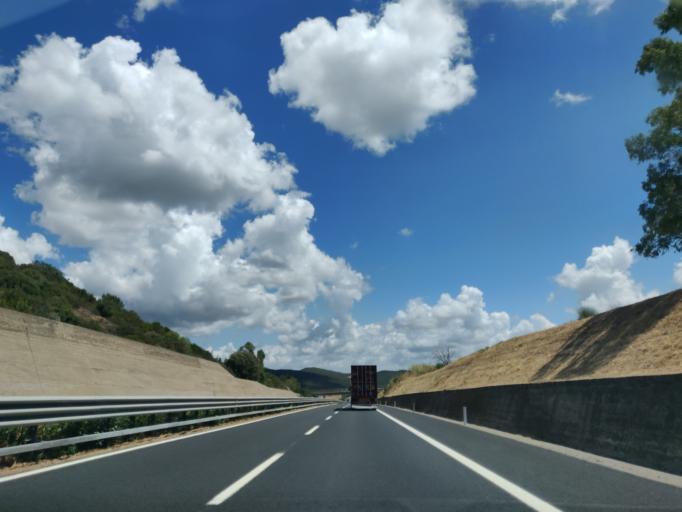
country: IT
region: Latium
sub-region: Citta metropolitana di Roma Capitale
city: Santa Marinella
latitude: 42.0435
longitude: 11.9099
